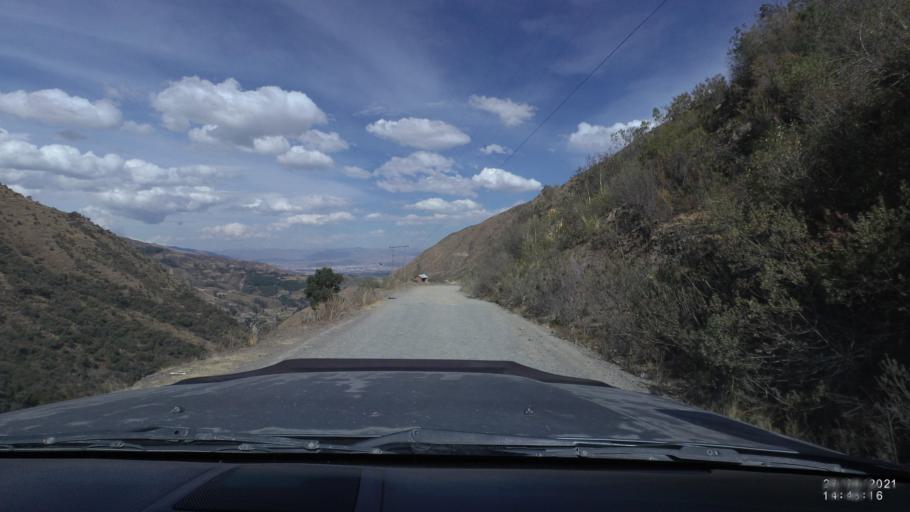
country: BO
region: Cochabamba
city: Sipe Sipe
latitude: -17.2780
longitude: -66.3197
